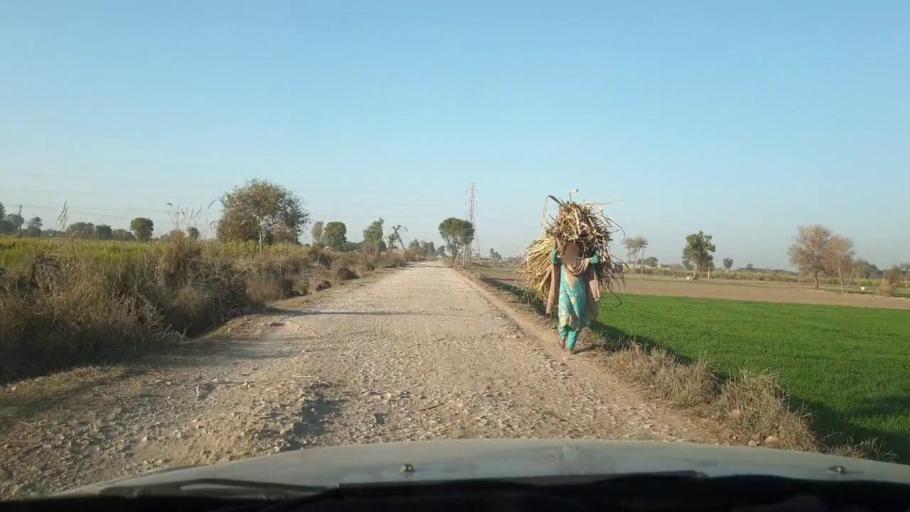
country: PK
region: Sindh
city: Ghotki
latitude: 27.9891
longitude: 69.2729
